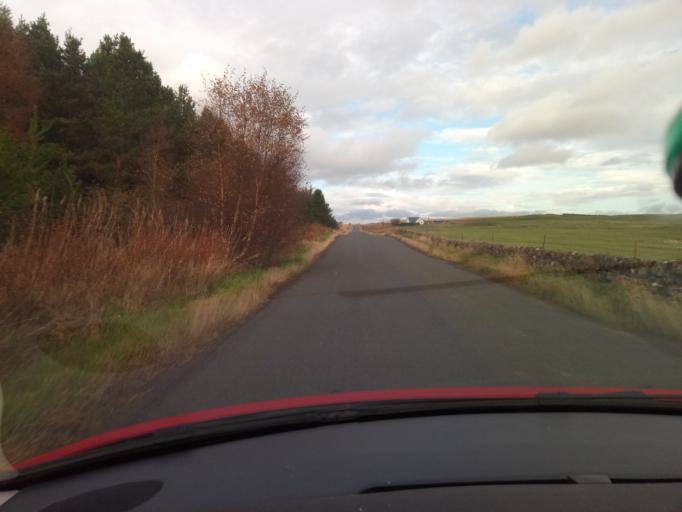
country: GB
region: Scotland
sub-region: South Lanarkshire
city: Carnwath
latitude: 55.7178
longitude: -3.5997
